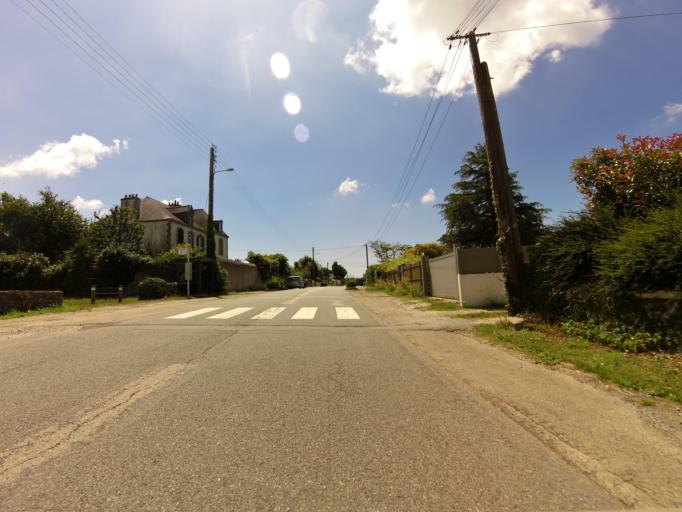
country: FR
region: Brittany
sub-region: Departement du Morbihan
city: Theix
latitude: 47.6146
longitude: -2.6839
